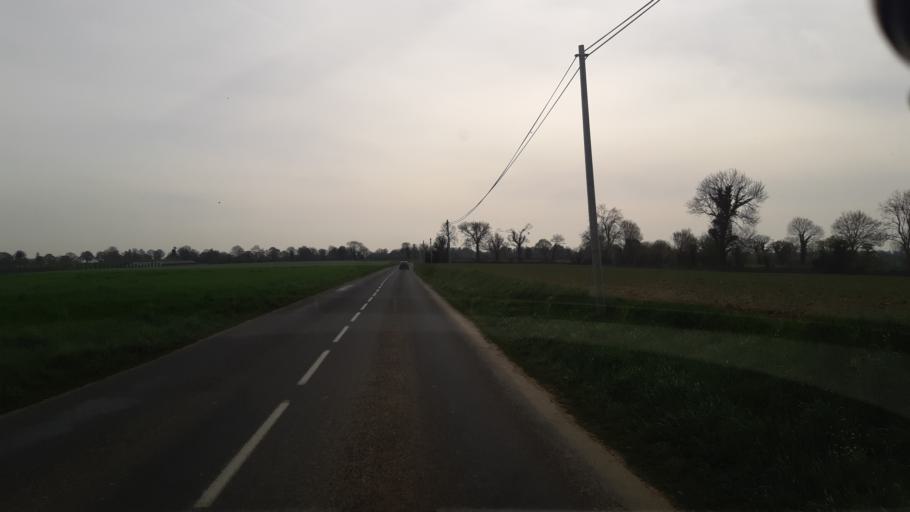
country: FR
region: Lower Normandy
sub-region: Departement de la Manche
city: Gavray
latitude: 48.9531
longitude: -1.3242
